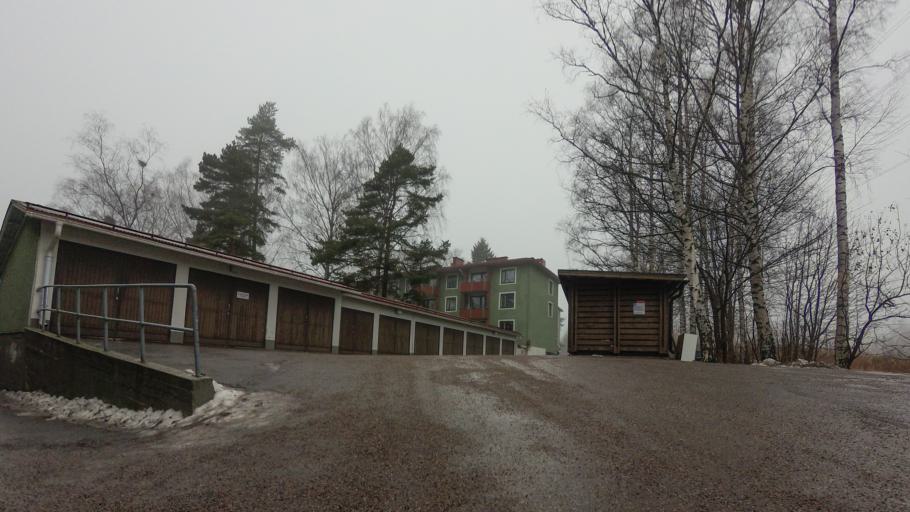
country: FI
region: Uusimaa
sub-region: Helsinki
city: Vantaa
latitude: 60.2082
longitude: 25.0468
